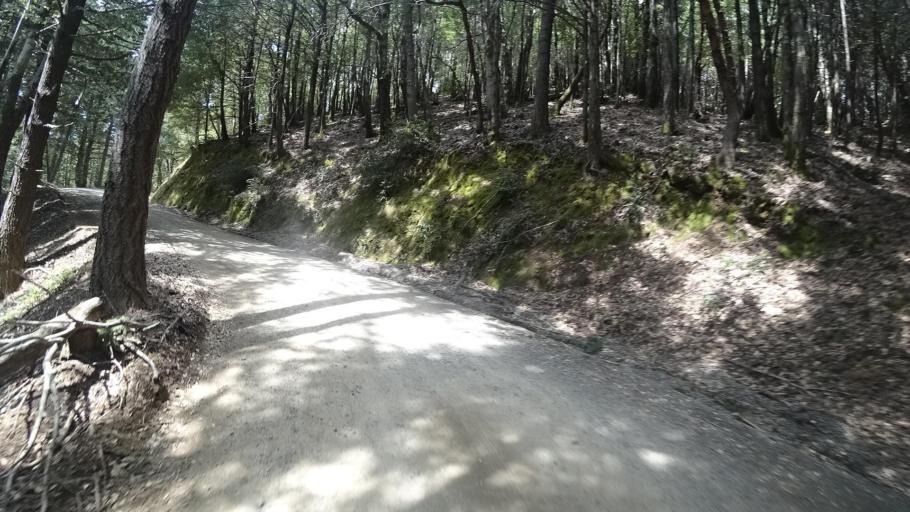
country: US
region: California
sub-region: Humboldt County
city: Redway
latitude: 40.0128
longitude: -123.9863
